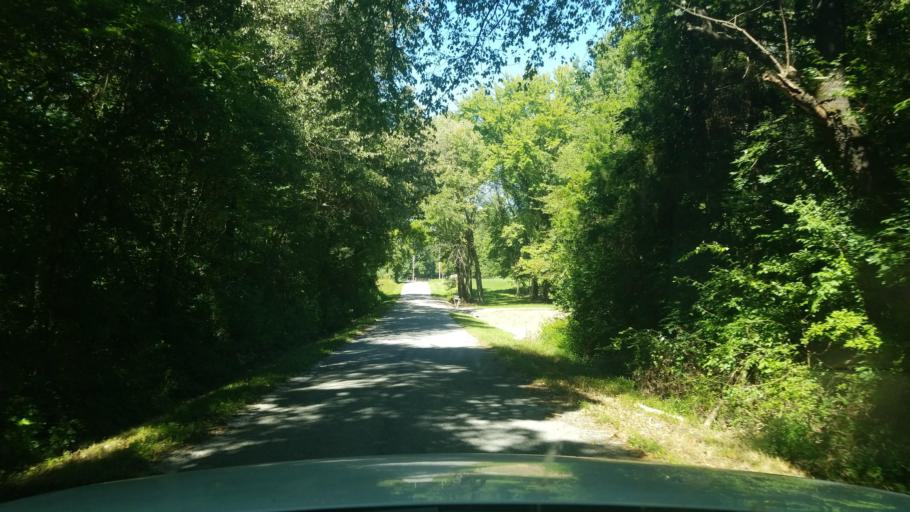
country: US
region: Illinois
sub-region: Saline County
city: Eldorado
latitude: 37.8501
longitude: -88.5165
